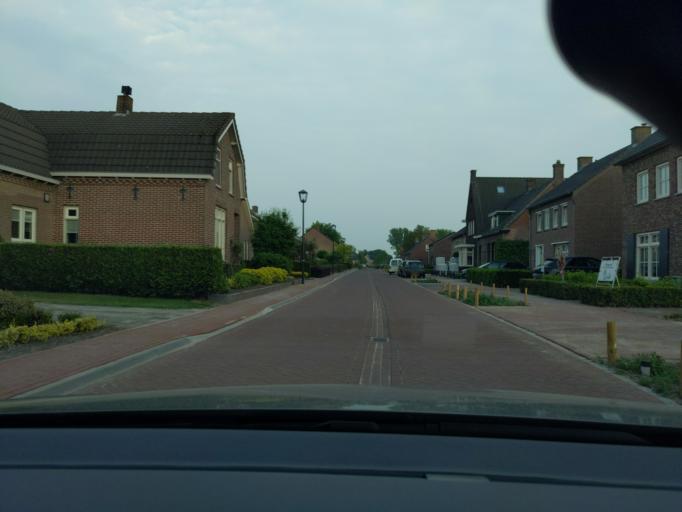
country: NL
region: North Brabant
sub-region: Gemeente Bladel en Netersel
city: Bladel
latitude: 51.3594
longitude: 5.1664
